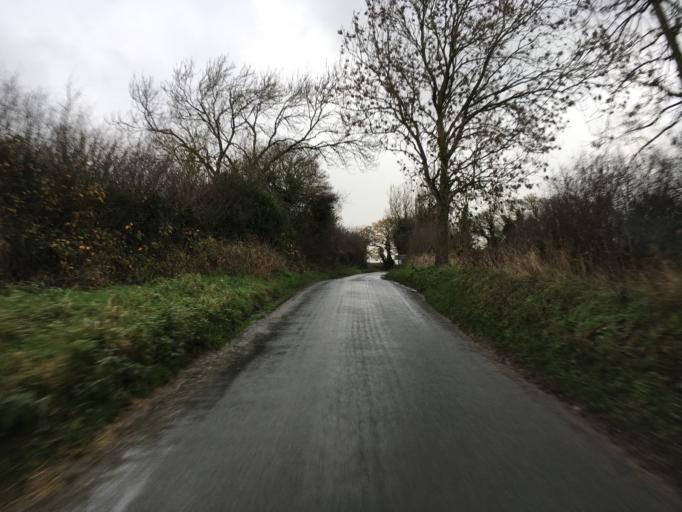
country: GB
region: England
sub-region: Wiltshire
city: Nettleton
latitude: 51.5102
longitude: -2.2637
